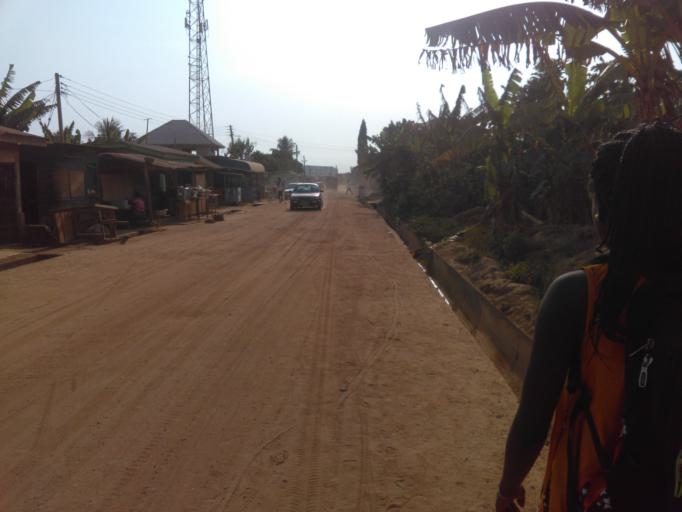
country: GH
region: Central
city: Cape Coast
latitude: 5.1102
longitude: -1.2951
